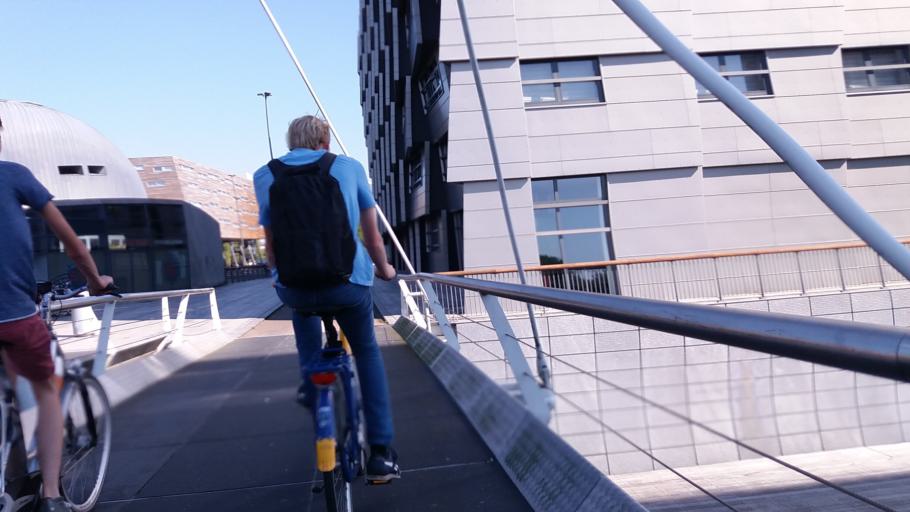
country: NL
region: Flevoland
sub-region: Gemeente Almere
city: Almere Stad
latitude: 52.3669
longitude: 5.2152
